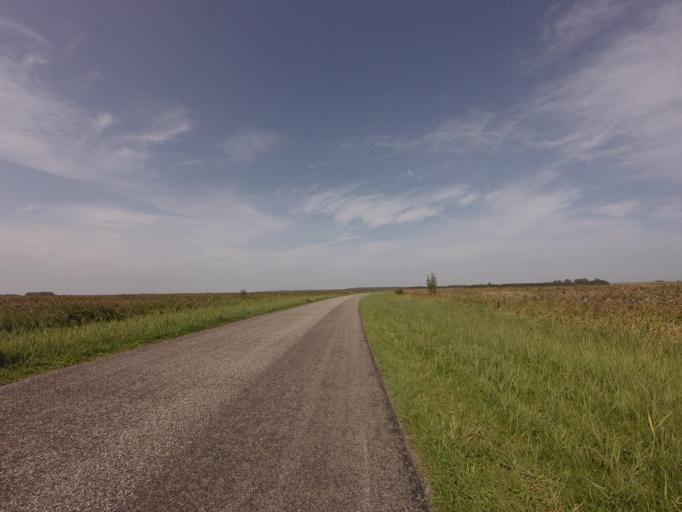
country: NL
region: Groningen
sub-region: Gemeente De Marne
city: Ulrum
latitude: 53.3486
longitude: 6.2673
